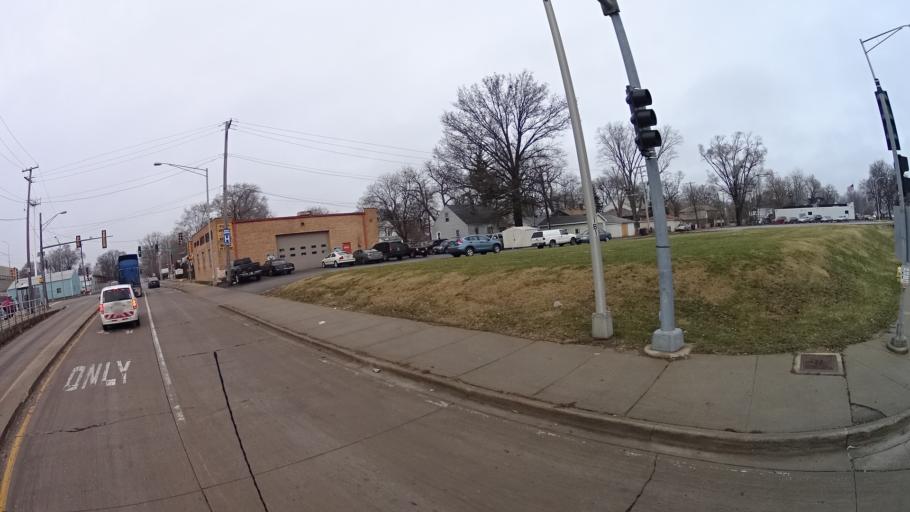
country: US
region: Illinois
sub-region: Cook County
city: East Hazel Crest
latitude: 41.5788
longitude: -87.6598
